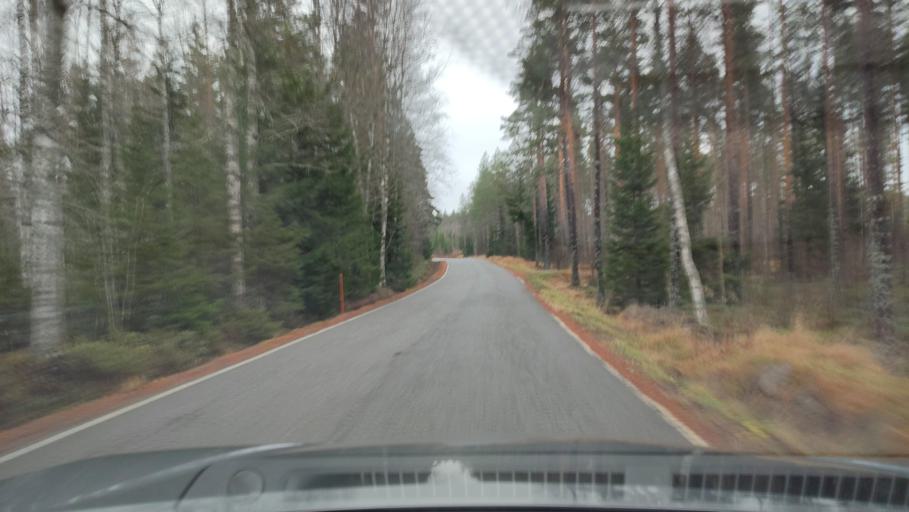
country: FI
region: Southern Ostrobothnia
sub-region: Suupohja
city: Isojoki
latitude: 62.1596
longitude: 21.8844
